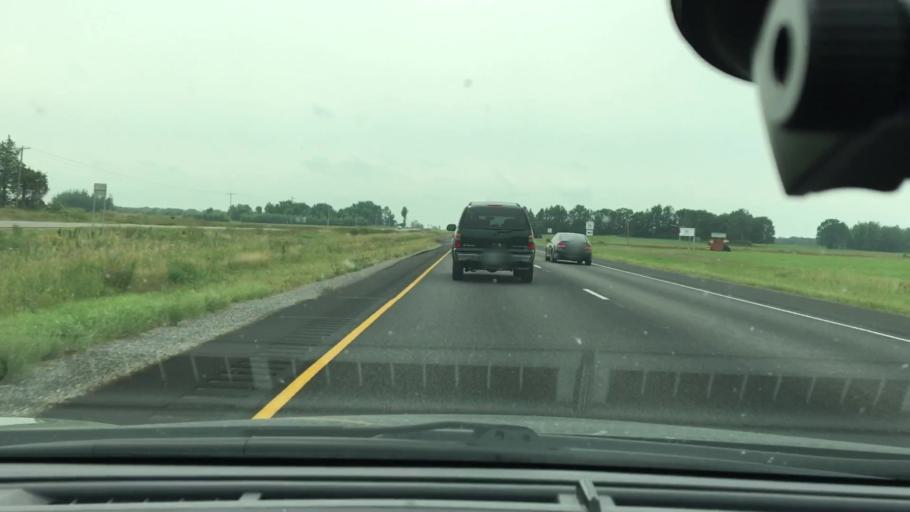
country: US
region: Minnesota
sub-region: Mille Lacs County
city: Milaca
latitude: 45.8539
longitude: -93.6623
